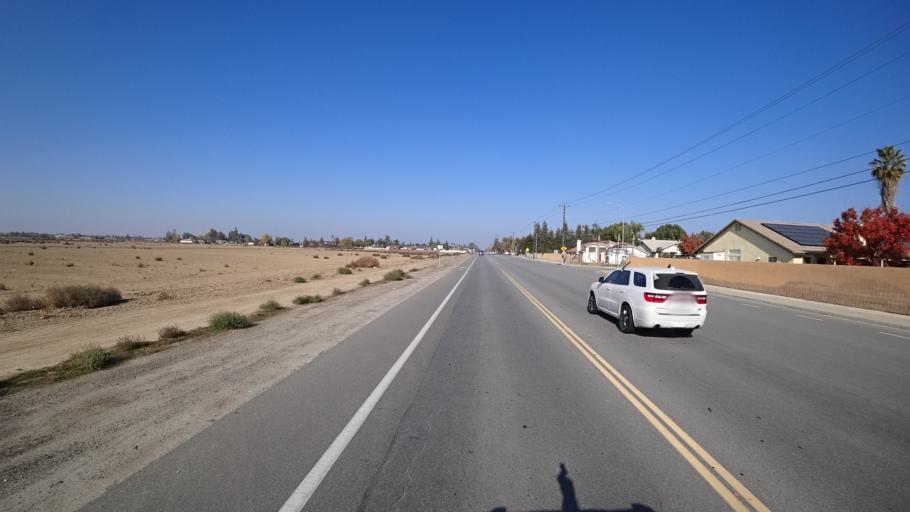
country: US
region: California
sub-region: Kern County
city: Rosedale
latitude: 35.3670
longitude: -119.1633
